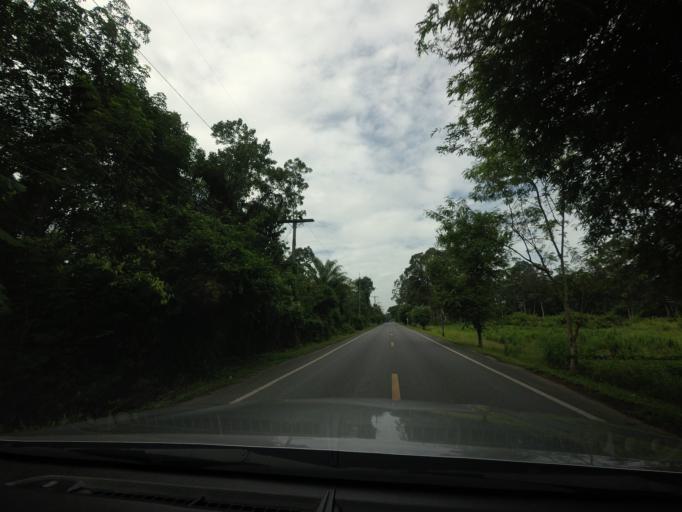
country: TH
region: Nakhon Si Thammarat
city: Phra Phrom
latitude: 8.2779
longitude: 99.9441
